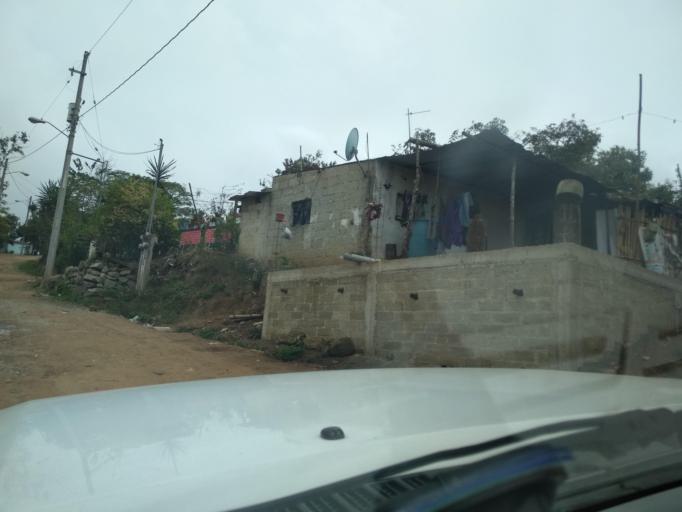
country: MX
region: Veracruz
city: El Castillo
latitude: 19.5380
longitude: -96.8342
